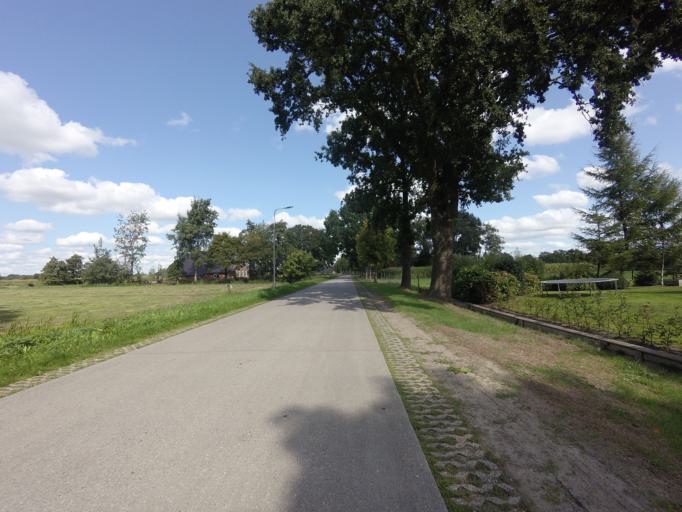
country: NL
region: Overijssel
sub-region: Gemeente Staphorst
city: Staphorst
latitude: 52.6030
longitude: 6.2539
